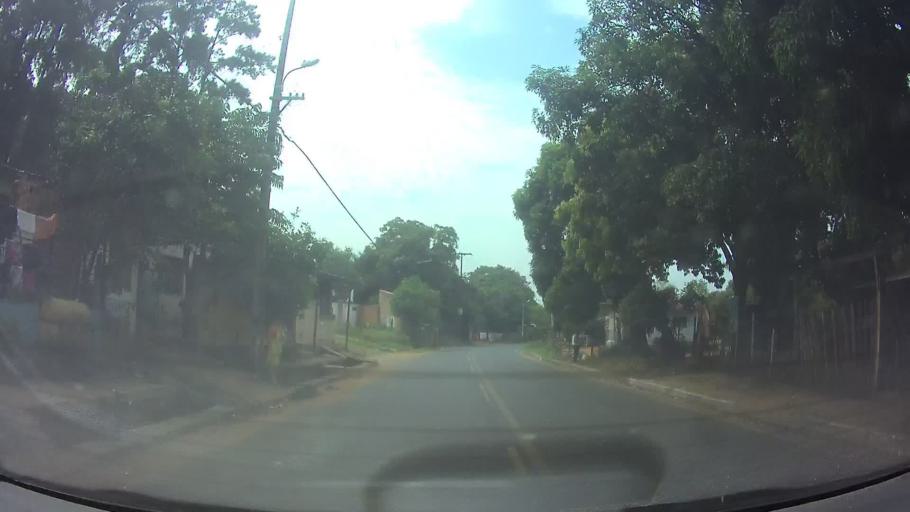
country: PY
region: Central
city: Fernando de la Mora
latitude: -25.2919
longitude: -57.5123
